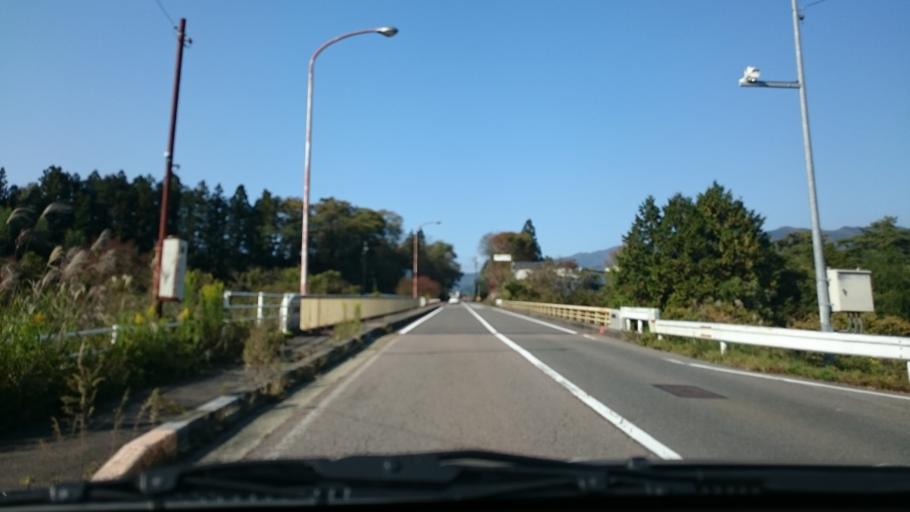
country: JP
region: Gifu
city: Nakatsugawa
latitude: 35.7359
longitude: 137.3438
